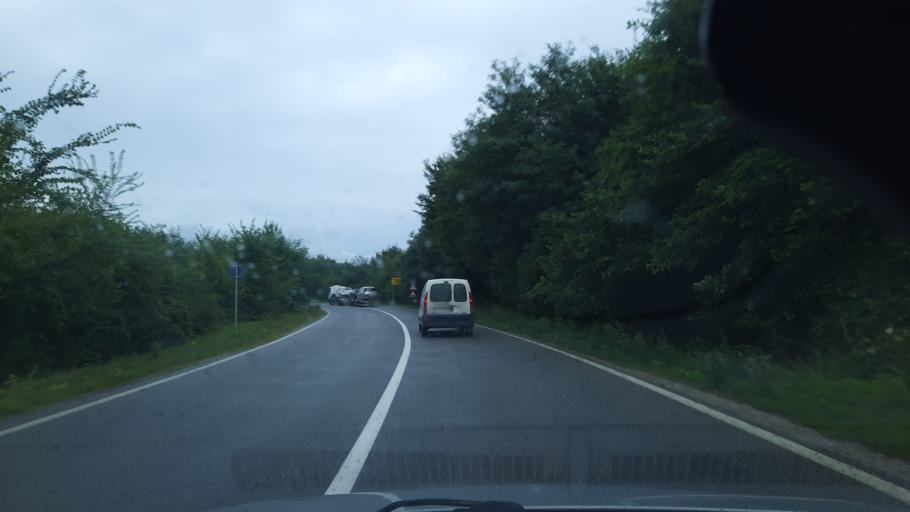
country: RS
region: Central Serbia
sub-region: Raski Okrug
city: Kraljevo
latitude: 43.7662
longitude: 20.8035
